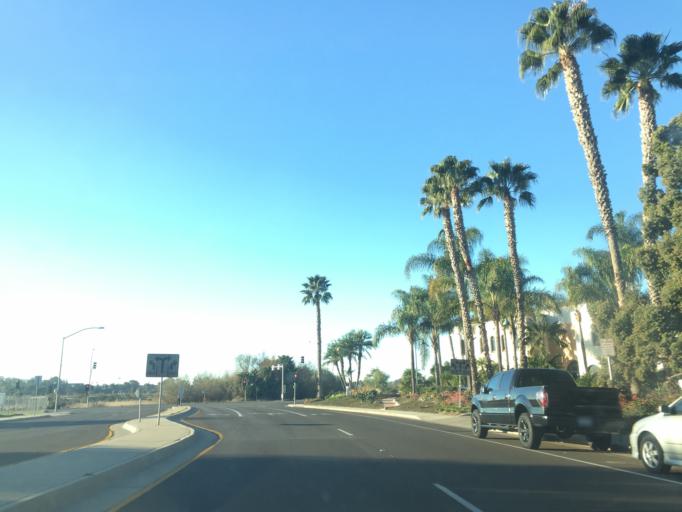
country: US
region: California
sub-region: Santa Barbara County
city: Isla Vista
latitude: 34.4318
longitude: -119.8545
